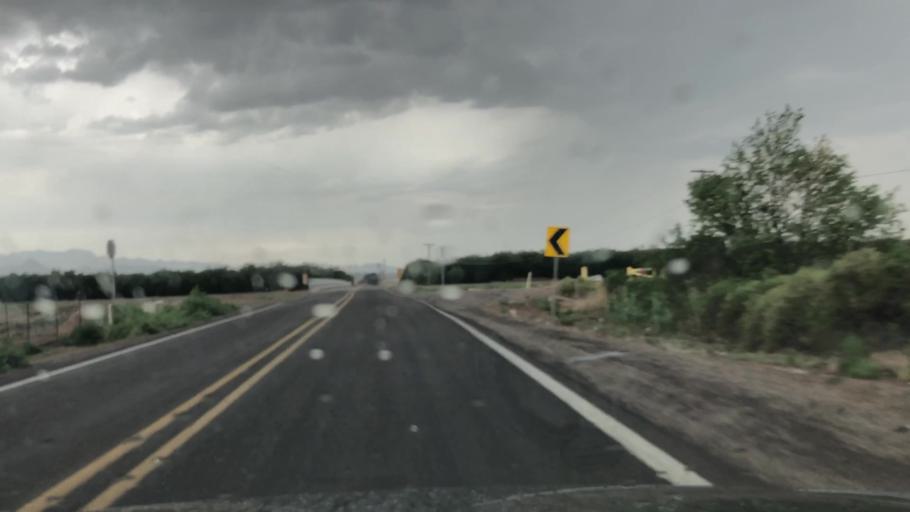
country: US
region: New Mexico
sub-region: Dona Ana County
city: Vado
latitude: 32.1128
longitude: -106.6700
